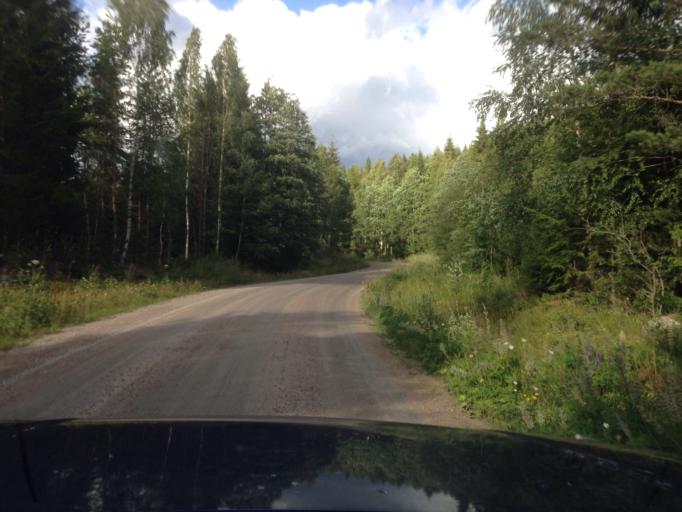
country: SE
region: Dalarna
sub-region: Ludvika Kommun
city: Abborrberget
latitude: 60.3080
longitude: 14.6501
